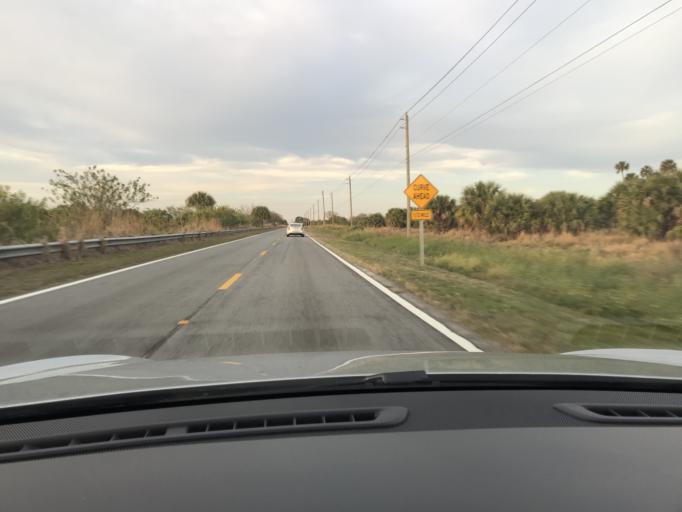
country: US
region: Florida
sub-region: Saint Lucie County
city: Lakewood Park
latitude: 27.5488
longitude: -80.4309
